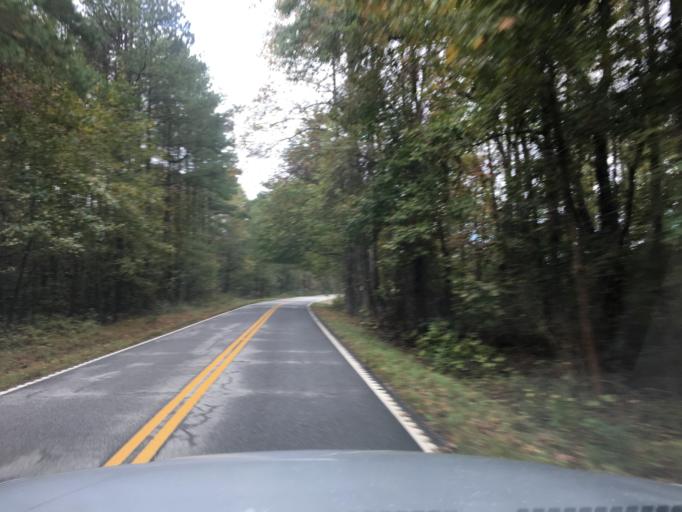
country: US
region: South Carolina
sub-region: Greenville County
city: Tigerville
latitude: 35.0610
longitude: -82.2763
